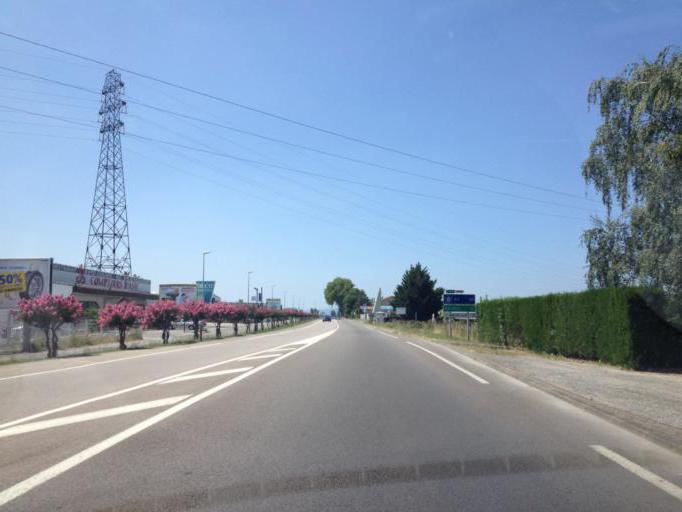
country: FR
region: Rhone-Alpes
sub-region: Departement de la Drome
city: Romans-sur-Isere
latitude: 45.0231
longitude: 5.0386
